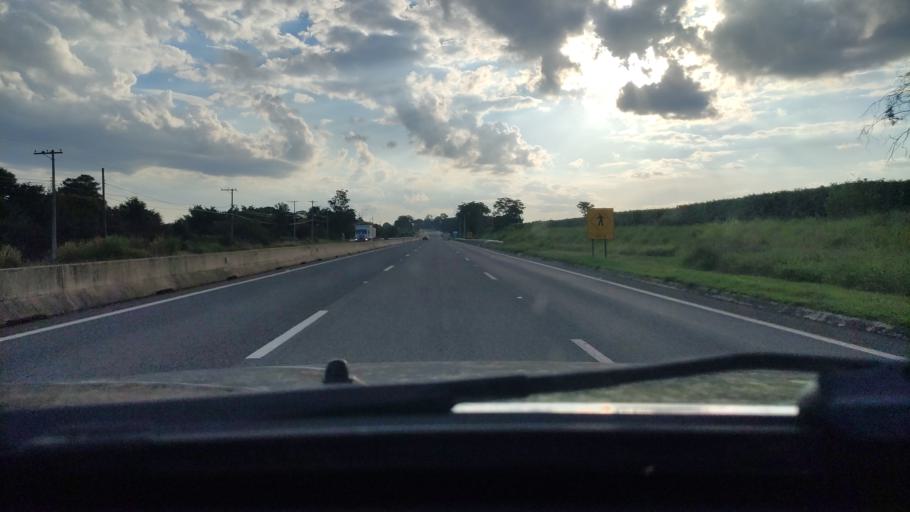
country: BR
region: Sao Paulo
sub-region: Mogi-Mirim
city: Mogi Mirim
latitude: -22.4504
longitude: -47.0721
